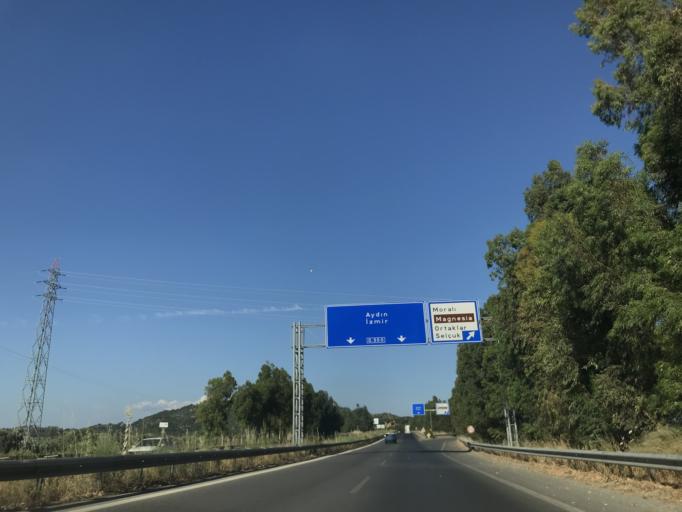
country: TR
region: Aydin
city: Ortaklar
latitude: 37.8340
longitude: 27.5256
